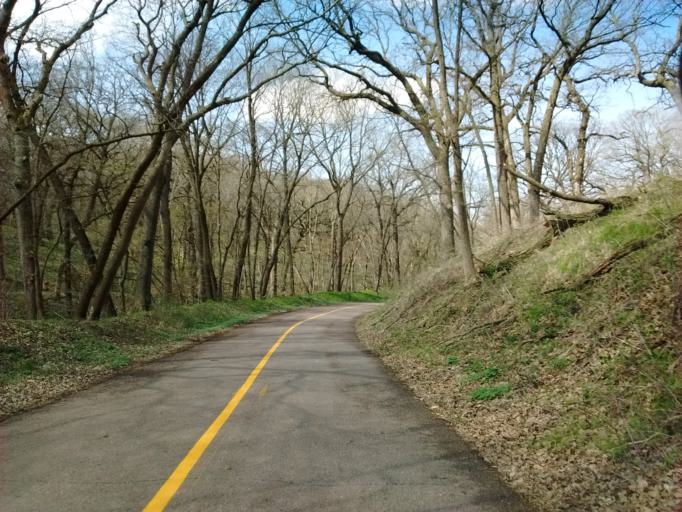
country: US
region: South Dakota
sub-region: Union County
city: North Sioux City
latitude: 42.5561
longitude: -96.4655
